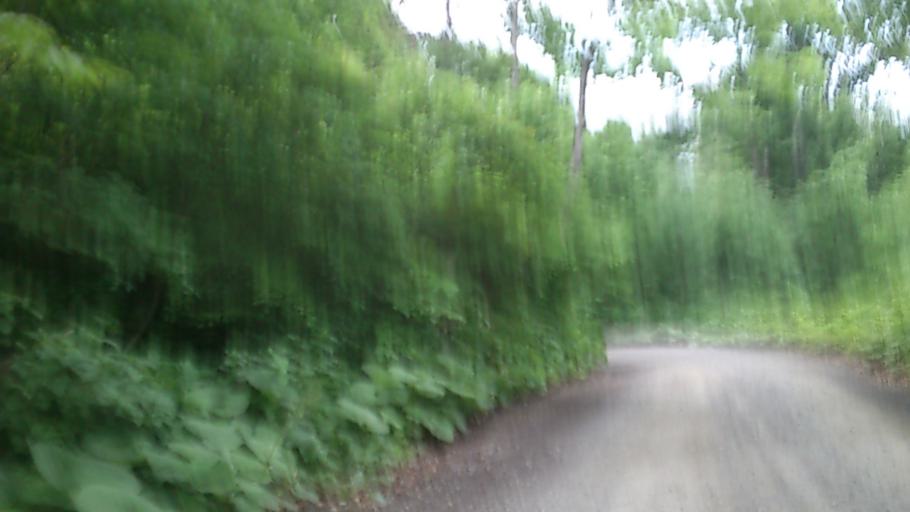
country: JP
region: Aomori
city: Hirosaki
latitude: 40.5588
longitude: 140.1667
